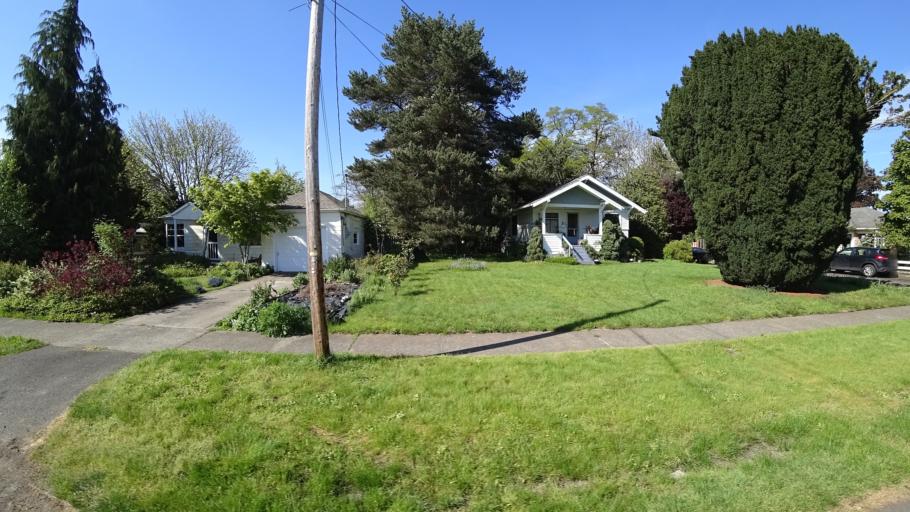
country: US
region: Oregon
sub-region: Washington County
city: Hillsboro
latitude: 45.5251
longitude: -122.9778
